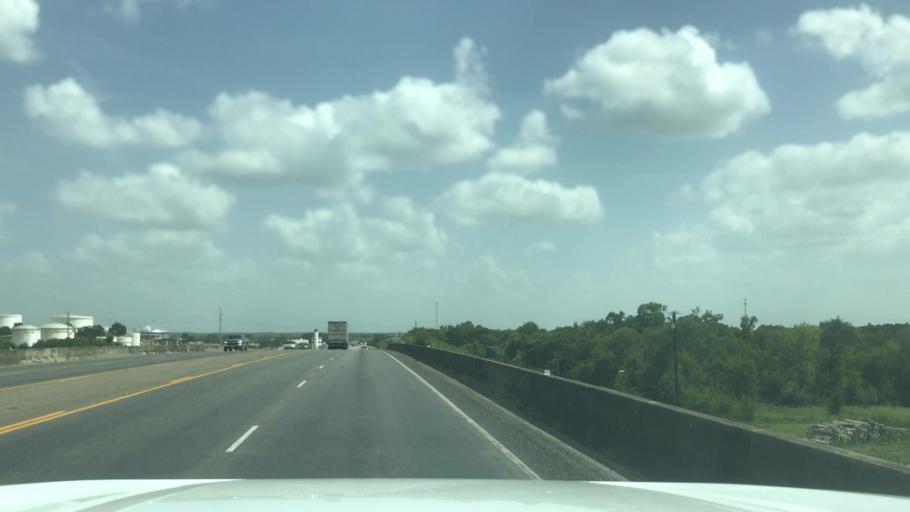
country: US
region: Texas
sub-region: Robertson County
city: Hearne
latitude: 30.8681
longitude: -96.5852
